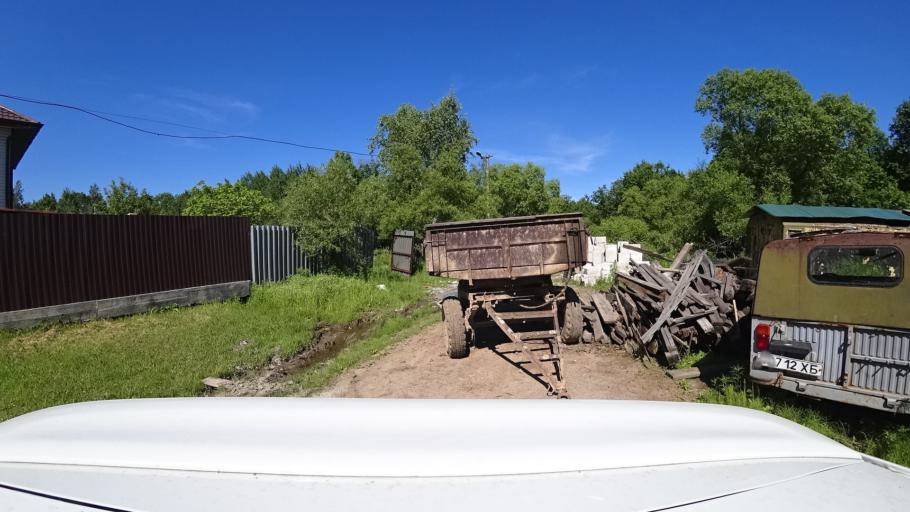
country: RU
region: Khabarovsk Krai
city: Topolevo
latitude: 48.5541
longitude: 135.2002
